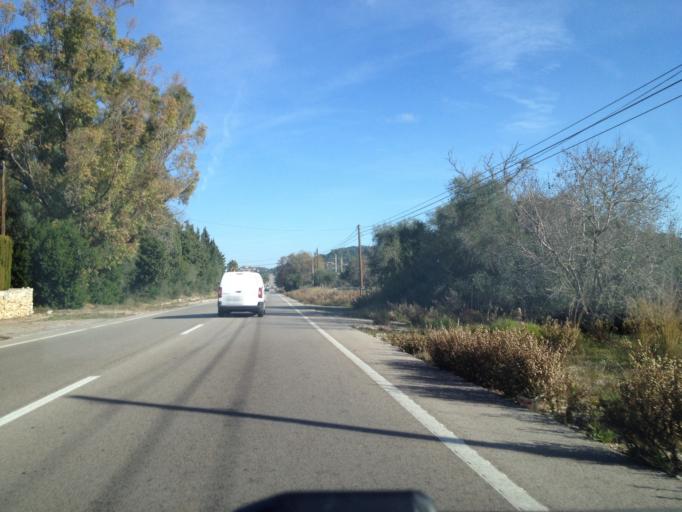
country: ES
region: Balearic Islands
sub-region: Illes Balears
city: Capdepera
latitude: 39.6756
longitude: 3.4057
